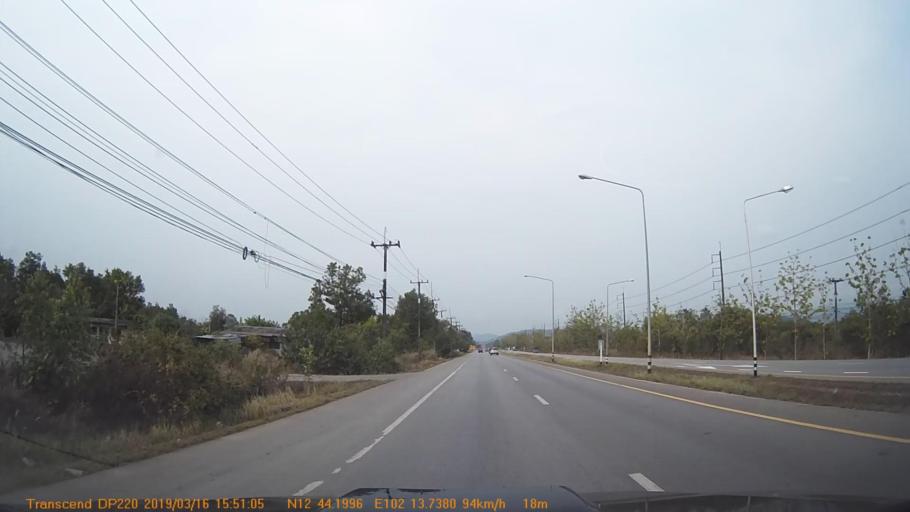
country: TH
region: Chanthaburi
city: Makham
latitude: 12.7368
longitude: 102.2291
